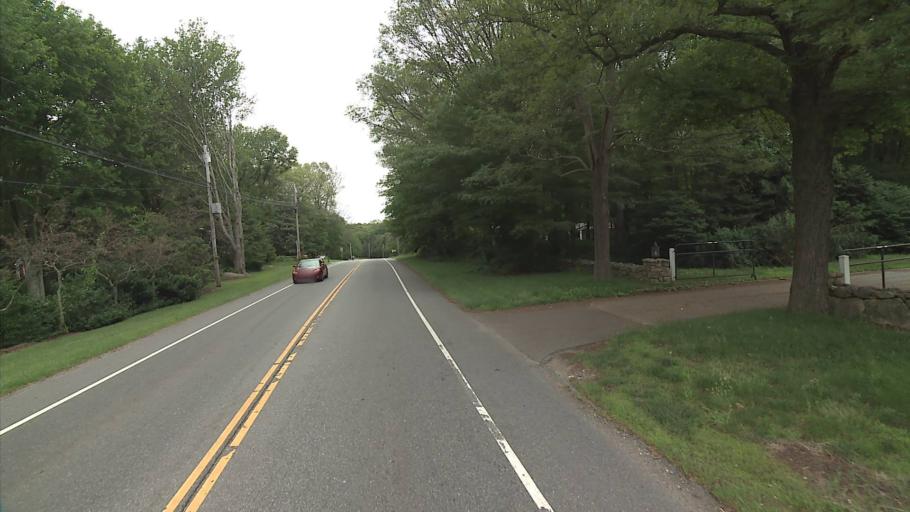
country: US
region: Connecticut
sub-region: New London County
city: Ledyard Center
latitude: 41.4064
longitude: -72.0222
